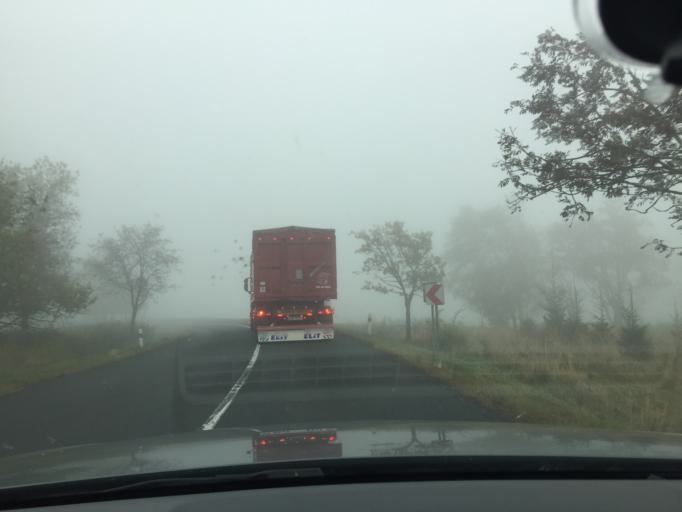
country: CZ
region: Ustecky
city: Libouchec
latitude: 50.7791
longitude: 13.9826
